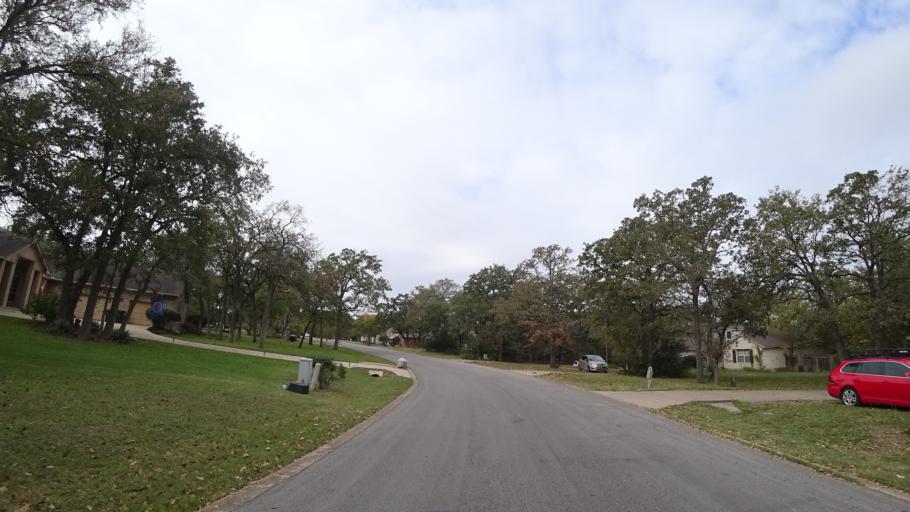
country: US
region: Texas
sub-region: Travis County
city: Shady Hollow
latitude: 30.1437
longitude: -97.8807
